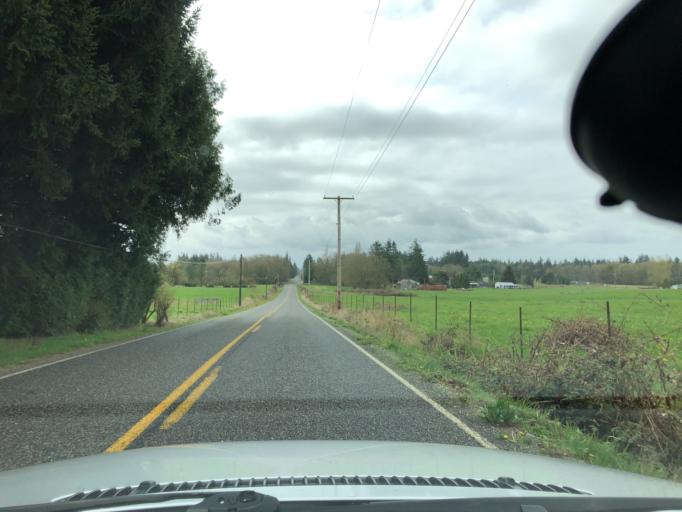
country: CA
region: British Columbia
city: Langley
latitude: 48.9749
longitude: -122.6159
